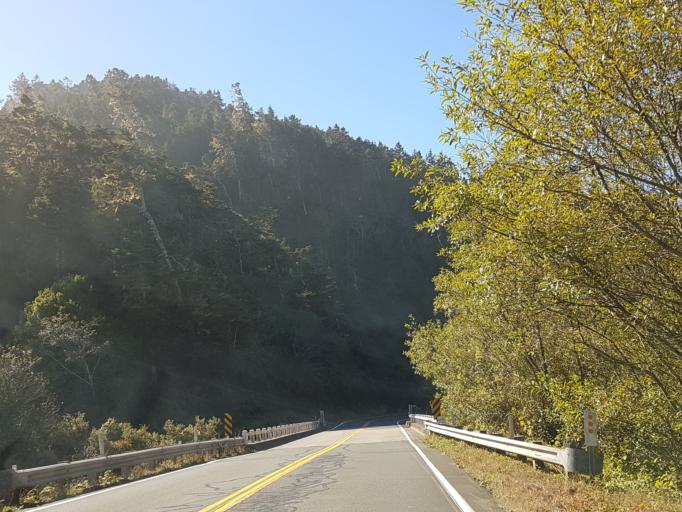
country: US
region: California
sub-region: Mendocino County
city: Boonville
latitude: 39.1025
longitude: -123.7014
